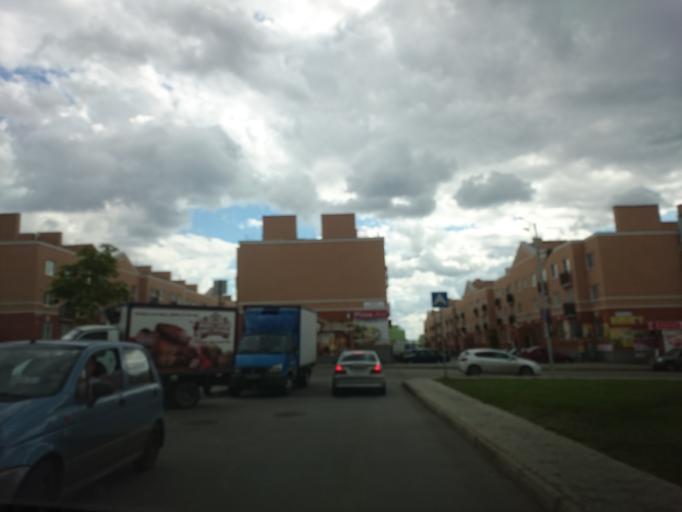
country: RU
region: Samara
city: Petra-Dubrava
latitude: 53.3202
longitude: 50.3083
